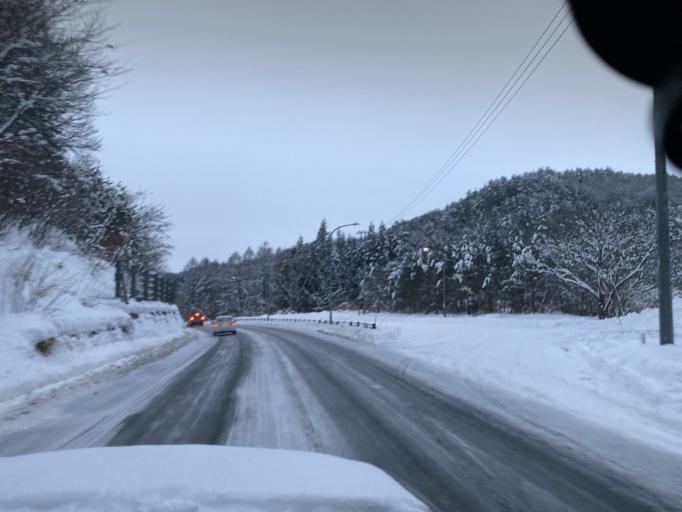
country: JP
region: Nagano
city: Omachi
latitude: 36.5358
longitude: 137.8643
